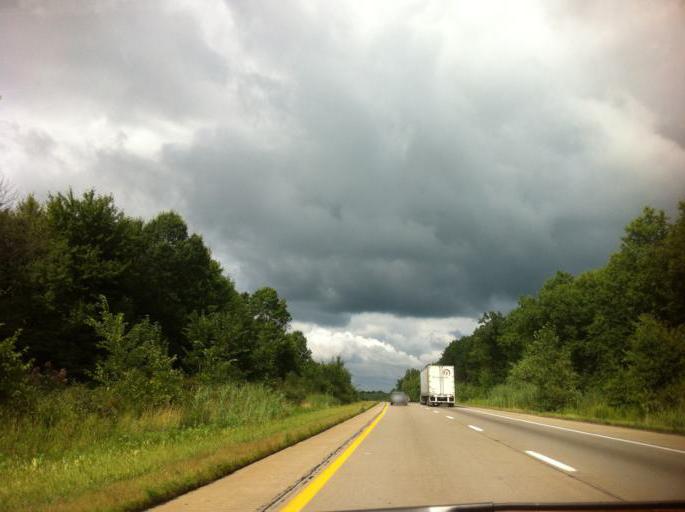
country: US
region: Pennsylvania
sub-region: Lawrence County
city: New Wilmington
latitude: 41.1864
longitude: -80.3504
